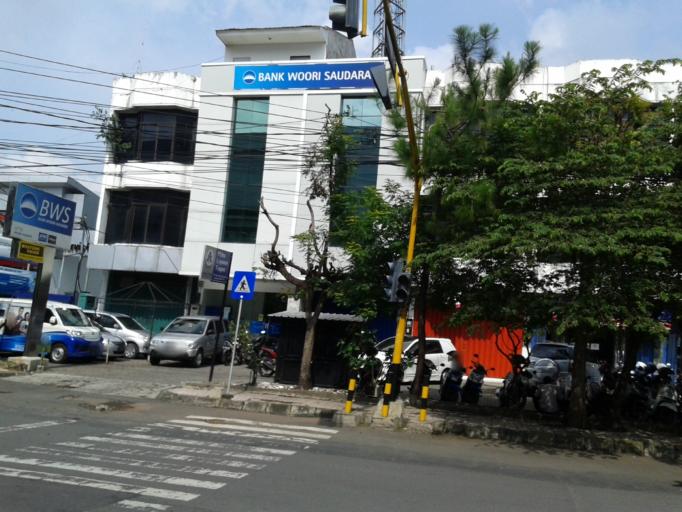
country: ID
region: East Java
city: Malang
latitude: -7.9665
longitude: 112.6318
